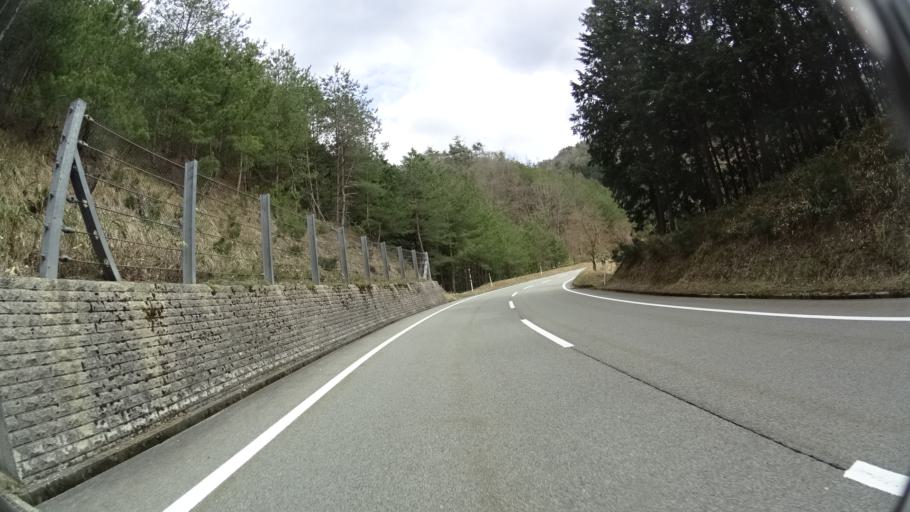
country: JP
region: Hyogo
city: Toyooka
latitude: 35.5037
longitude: 134.9033
